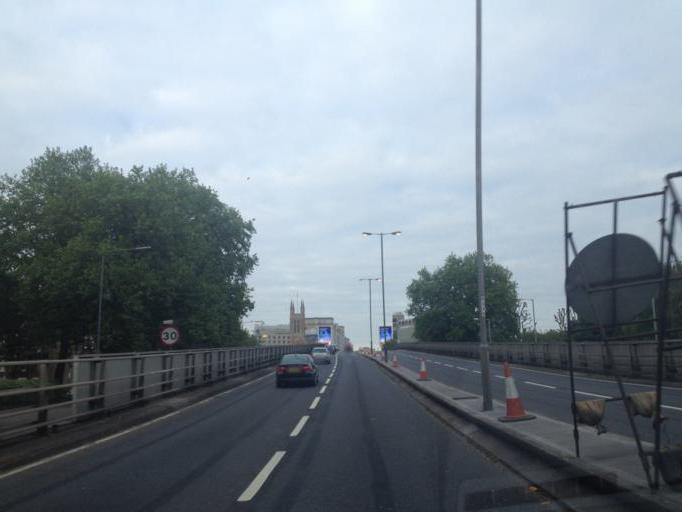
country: GB
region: England
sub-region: Greater London
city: Hammersmith
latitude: 51.4910
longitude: -0.2309
